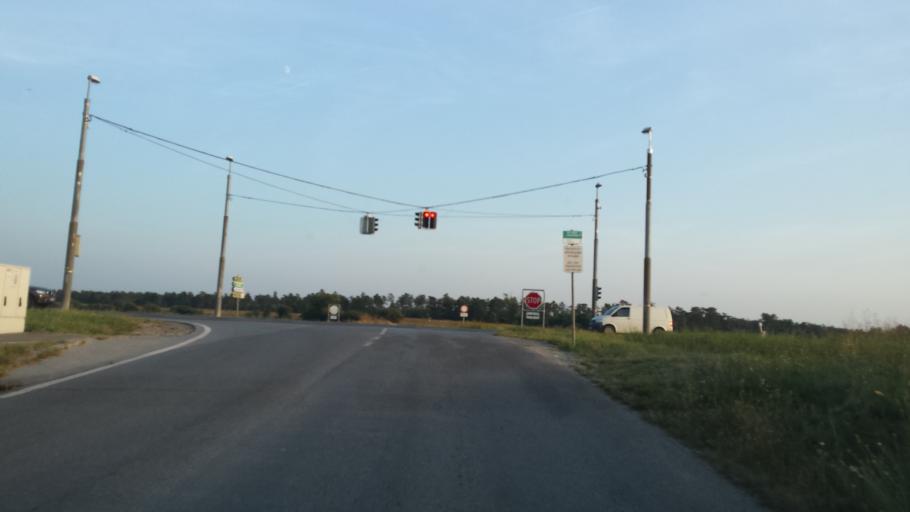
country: AT
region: Lower Austria
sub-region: Politischer Bezirk Ganserndorf
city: Parbasdorf
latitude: 48.3095
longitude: 16.5961
